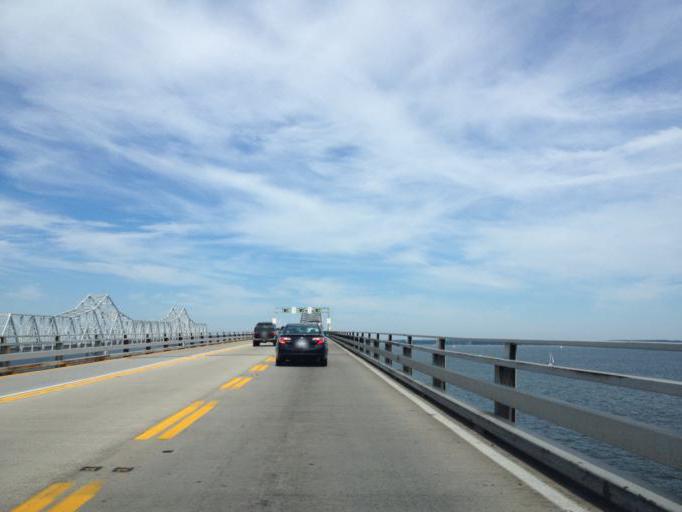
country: US
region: Maryland
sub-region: Queen Anne's County
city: Stevensville
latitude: 38.9876
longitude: -76.3521
